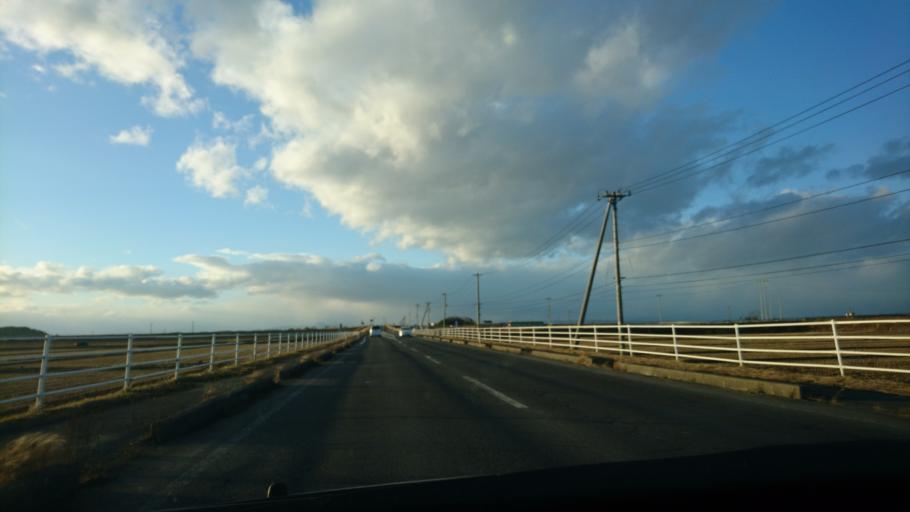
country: JP
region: Miyagi
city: Wakuya
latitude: 38.7177
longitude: 141.1619
